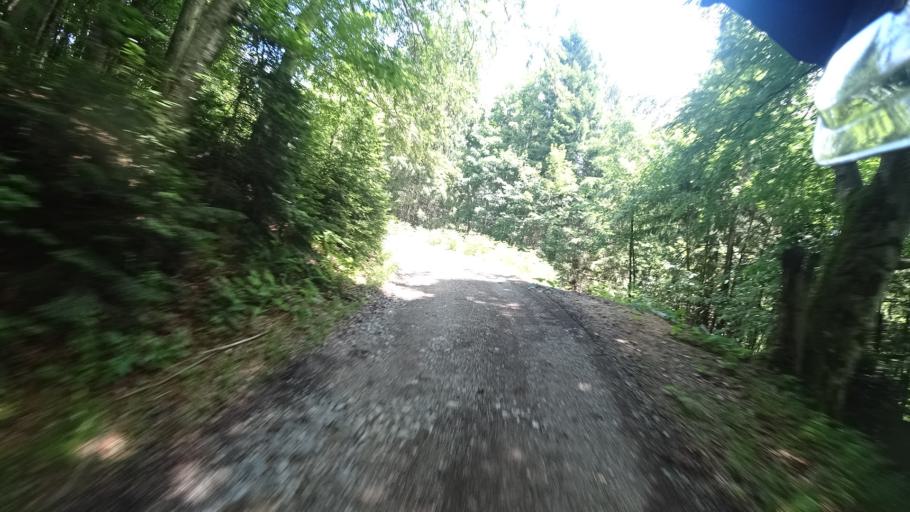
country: SI
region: Osilnica
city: Osilnica
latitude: 45.4663
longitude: 14.7348
